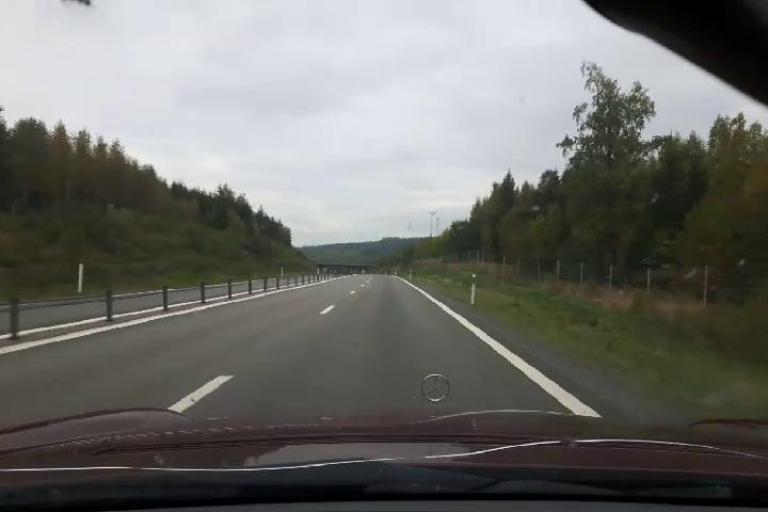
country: SE
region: Vaesternorrland
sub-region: Haernoesands Kommun
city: Haernoesand
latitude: 62.7606
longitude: 17.9048
